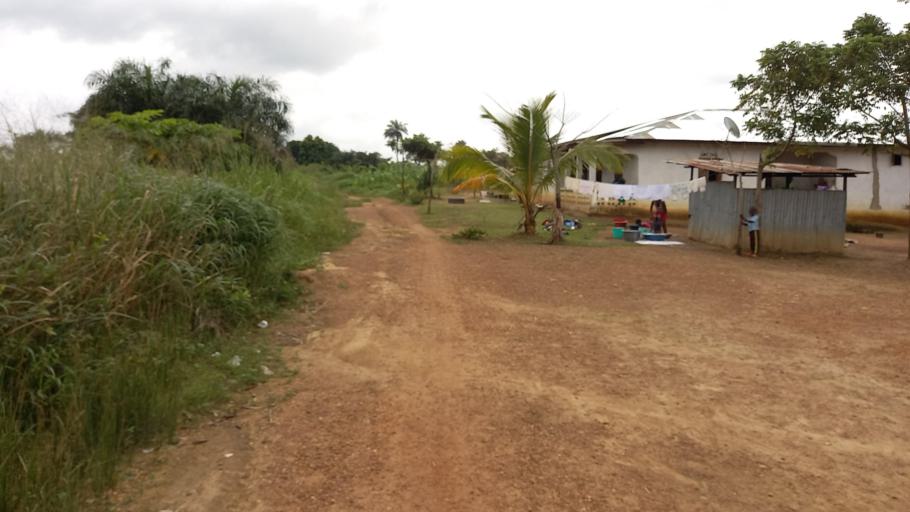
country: SL
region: Eastern Province
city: Kailahun
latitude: 8.2880
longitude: -10.5704
